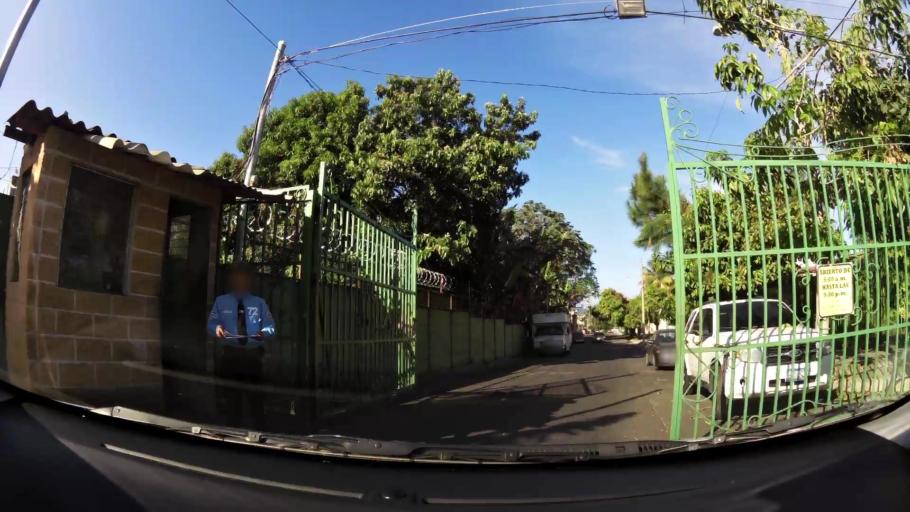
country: SV
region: La Libertad
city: Santa Tecla
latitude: 13.6825
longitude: -89.2881
